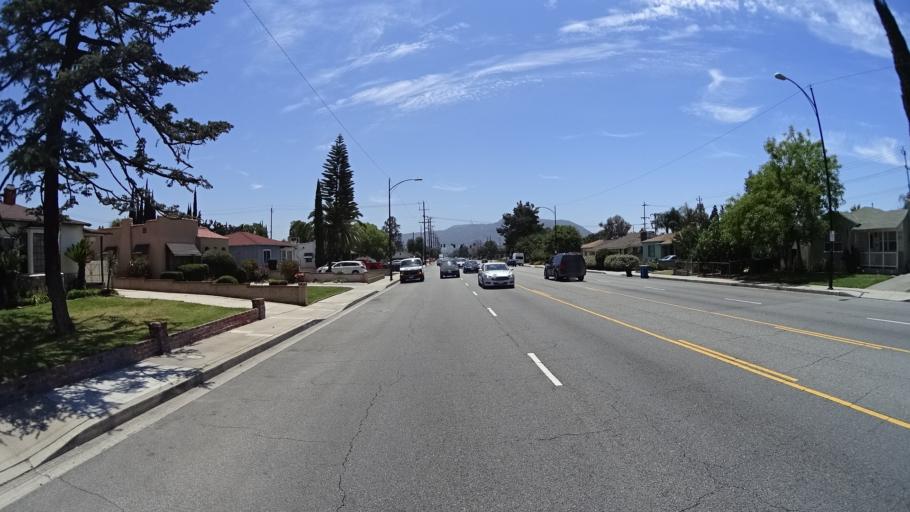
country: US
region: California
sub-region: Los Angeles County
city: Burbank
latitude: 34.1768
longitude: -118.3371
